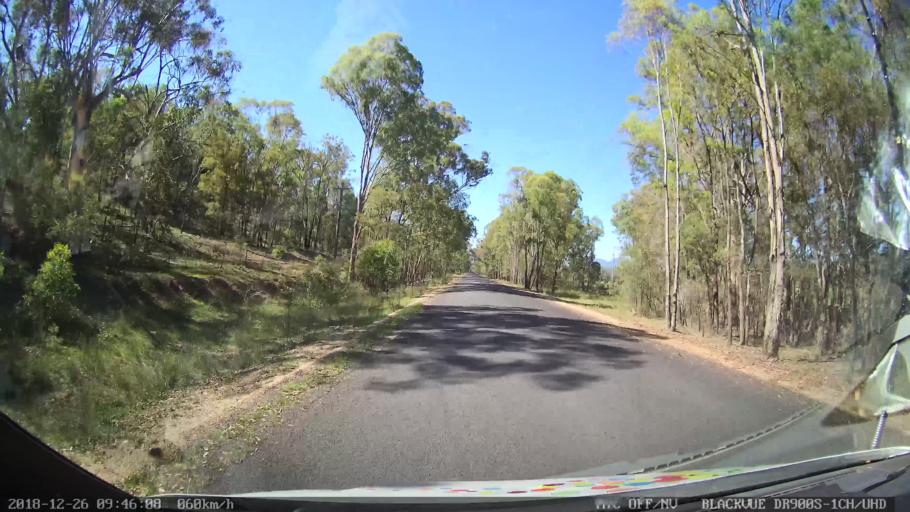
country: AU
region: New South Wales
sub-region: Mid-Western Regional
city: Kandos
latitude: -32.9672
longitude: 150.1060
